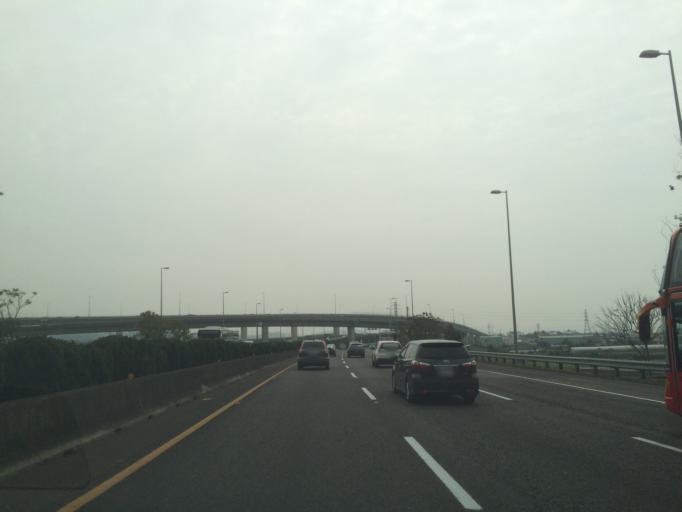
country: TW
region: Taiwan
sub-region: Taichung City
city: Taichung
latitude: 24.0534
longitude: 120.6774
